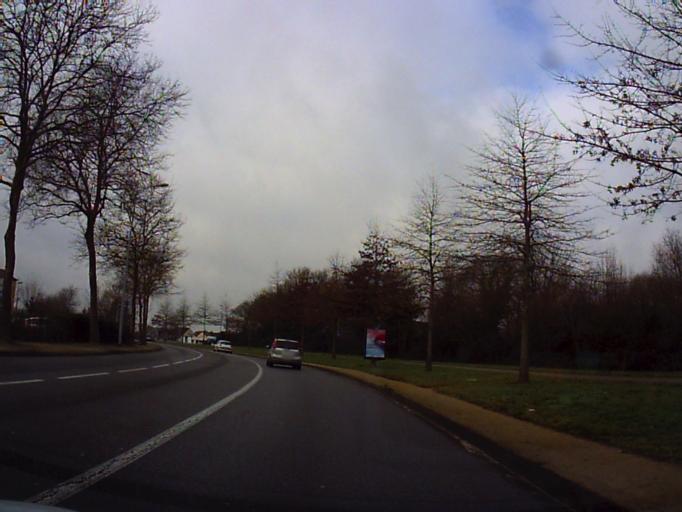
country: FR
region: Brittany
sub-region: Departement du Morbihan
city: Vannes
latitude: 47.6673
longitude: -2.7757
